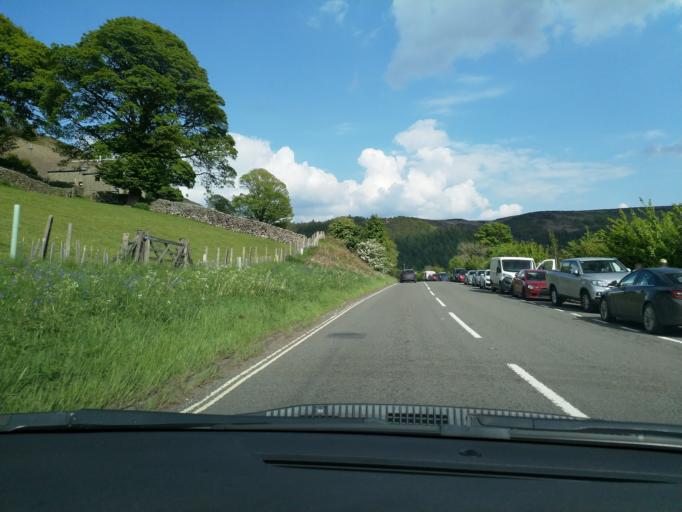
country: GB
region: England
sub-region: Derbyshire
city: Hope Valley
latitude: 53.3744
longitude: -1.7057
